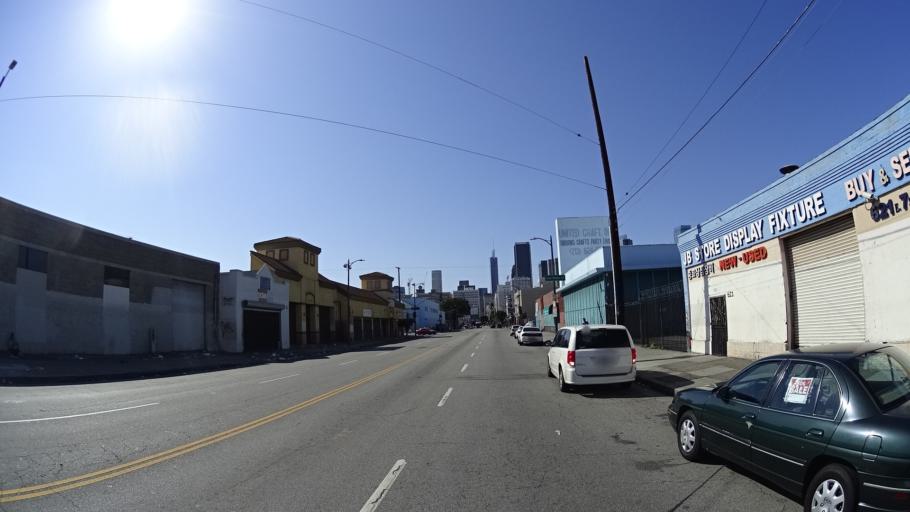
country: US
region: California
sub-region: Los Angeles County
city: Los Angeles
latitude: 34.0401
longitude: -118.2459
